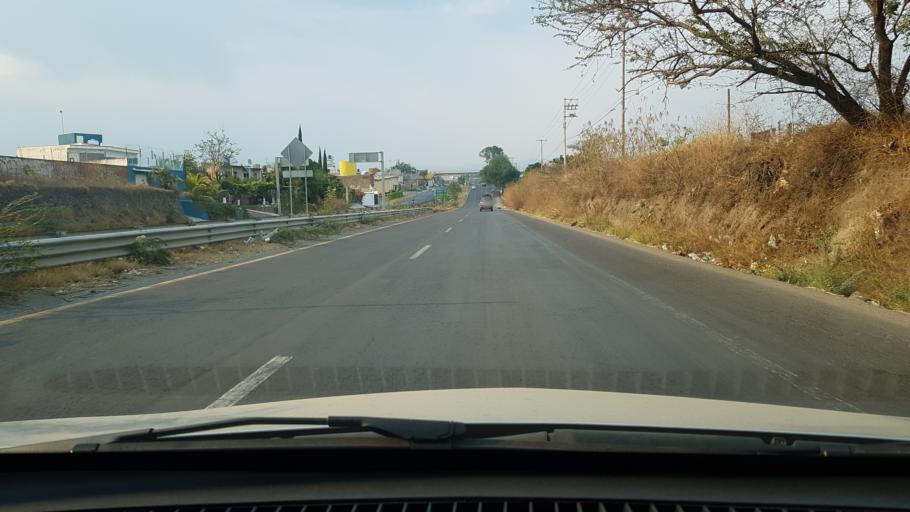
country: MX
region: Morelos
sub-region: Yecapixtla
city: Juan Morales
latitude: 18.8002
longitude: -98.9156
